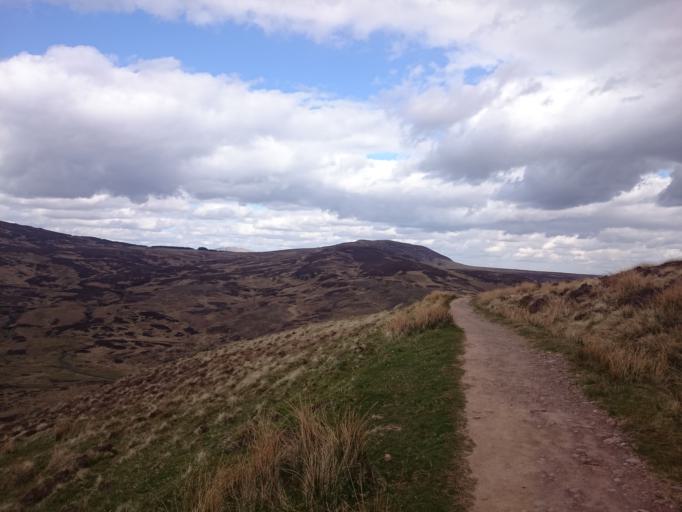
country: GB
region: Scotland
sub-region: West Dunbartonshire
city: Balloch
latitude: 56.0999
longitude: -4.5212
